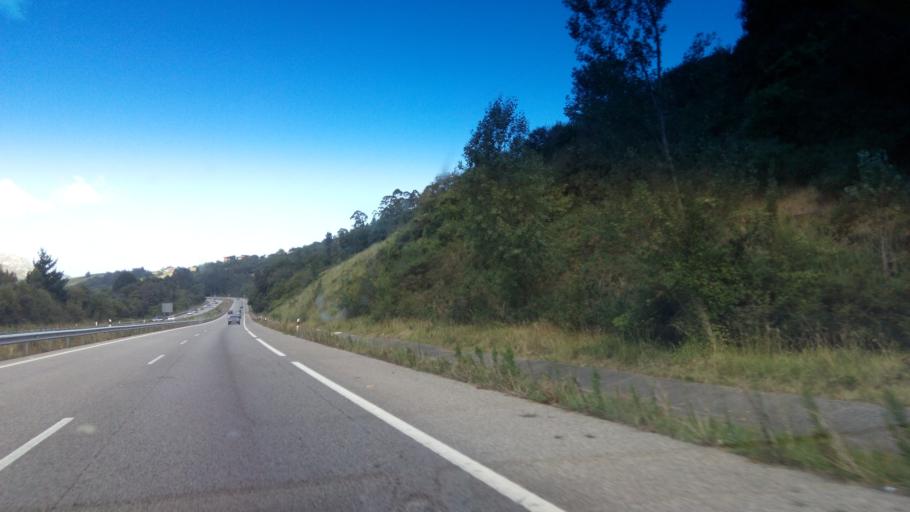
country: ES
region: Asturias
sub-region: Province of Asturias
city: Ribadesella
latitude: 43.4367
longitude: -5.0698
